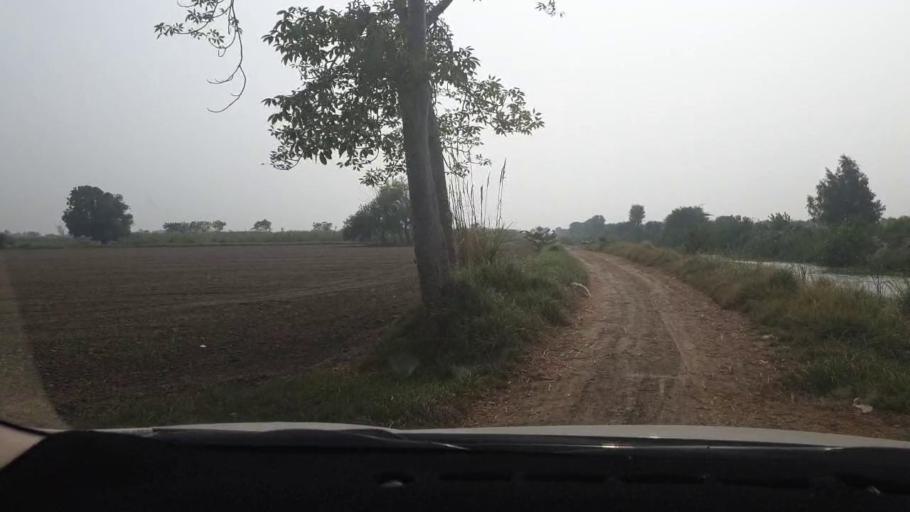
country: PK
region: Sindh
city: Tando Muhammad Khan
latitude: 25.0578
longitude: 68.5085
